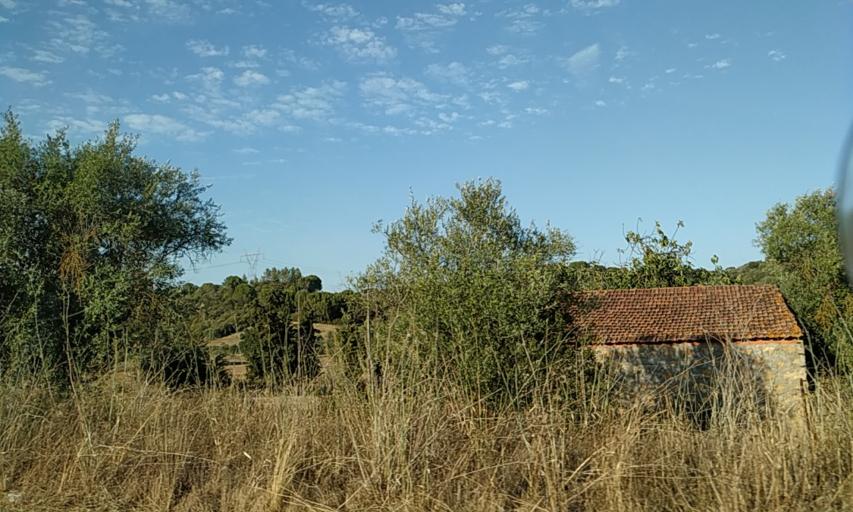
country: PT
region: Santarem
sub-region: Alcanena
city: Alcanena
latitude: 39.3696
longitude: -8.6584
